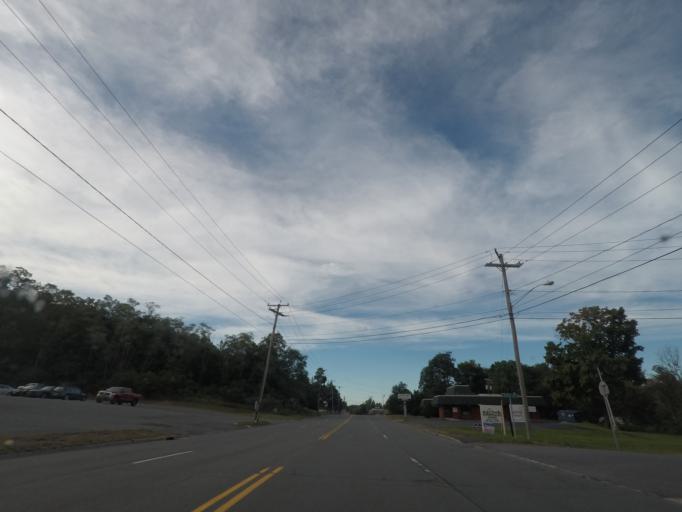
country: US
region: New York
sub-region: Rensselaer County
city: East Greenbush
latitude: 42.5671
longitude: -73.6840
